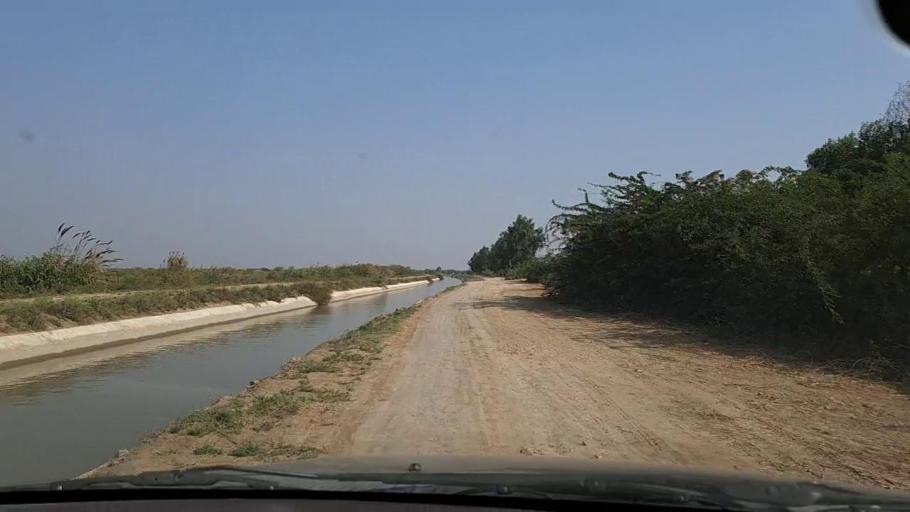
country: PK
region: Sindh
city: Mirpur Sakro
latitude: 24.3420
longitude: 67.7045
